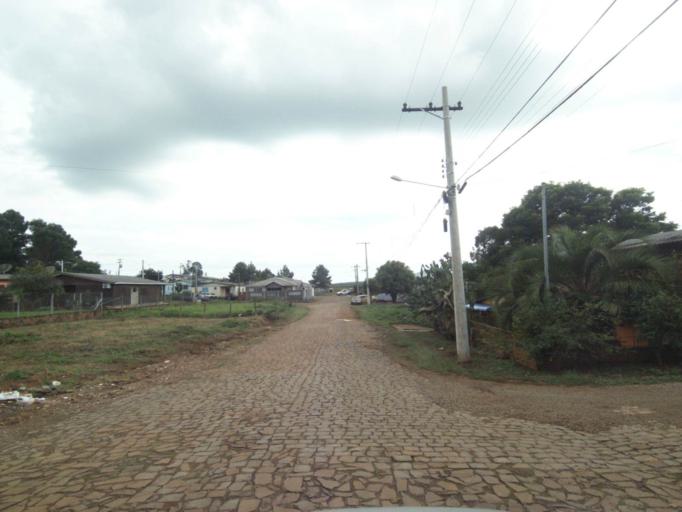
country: BR
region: Rio Grande do Sul
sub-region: Lagoa Vermelha
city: Lagoa Vermelha
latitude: -28.2234
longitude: -51.5095
